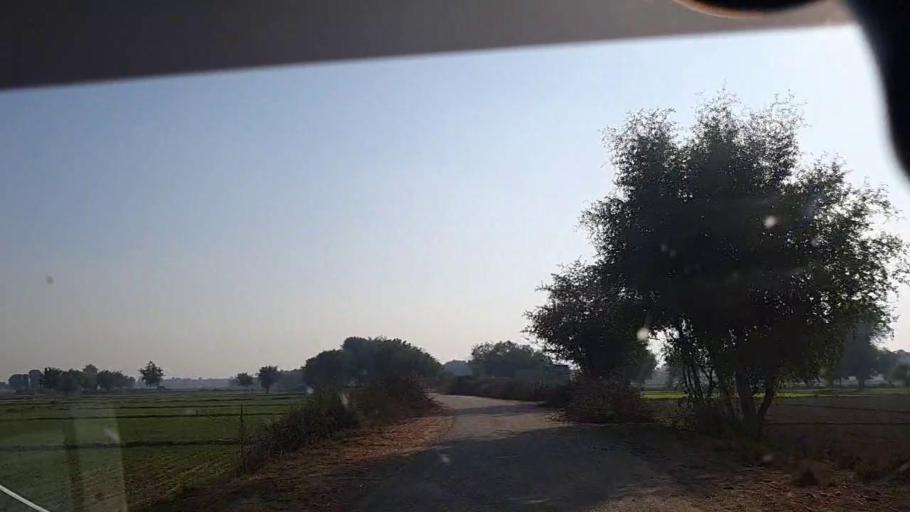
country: PK
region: Sindh
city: Hingorja
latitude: 27.2286
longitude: 68.2689
